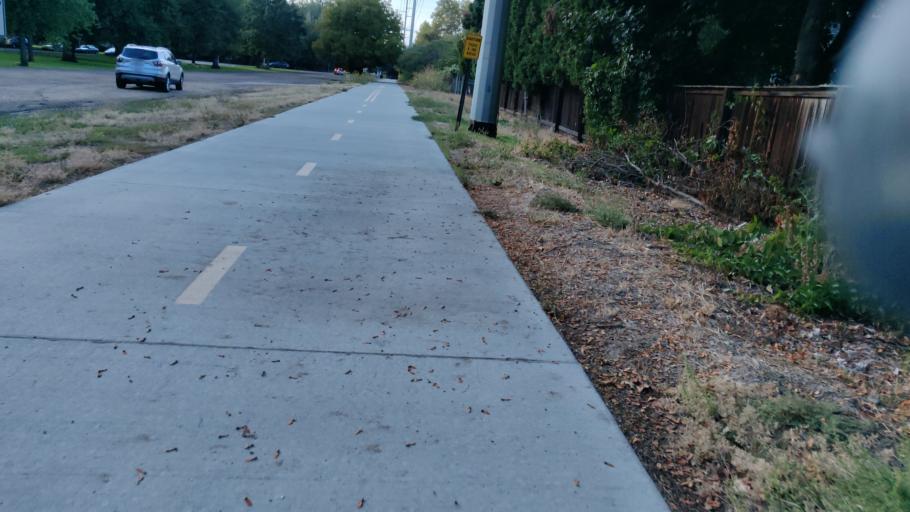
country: US
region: Idaho
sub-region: Ada County
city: Boise
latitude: 43.6034
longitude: -116.1829
